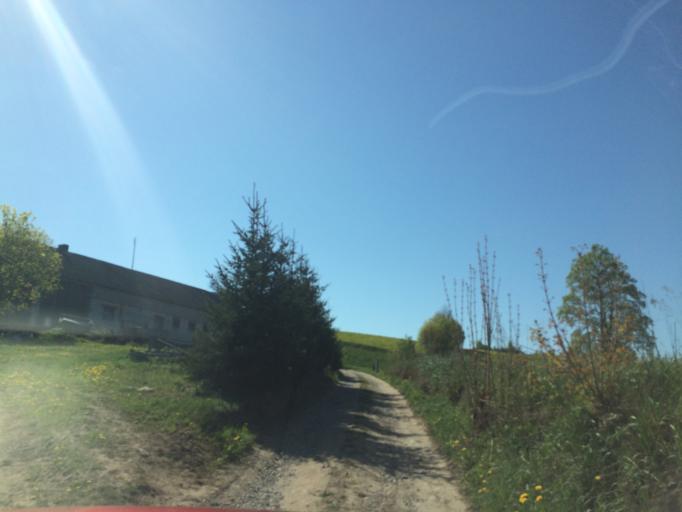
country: PL
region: Warmian-Masurian Voivodeship
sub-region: Powiat nowomiejski
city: Biskupiec
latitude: 53.4882
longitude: 19.4754
